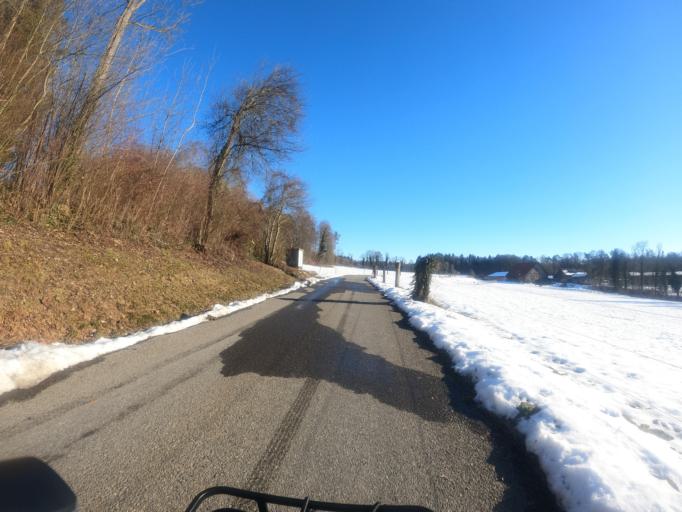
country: CH
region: Aargau
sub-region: Bezirk Bremgarten
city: Oberlunkhofen
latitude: 47.3228
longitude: 8.3941
